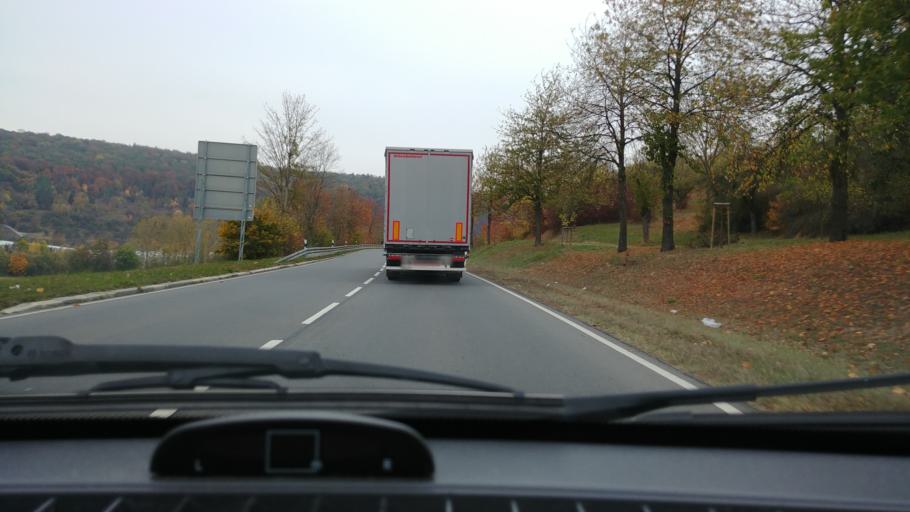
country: DE
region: Baden-Wuerttemberg
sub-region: Regierungsbezirk Stuttgart
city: Bad Mergentheim
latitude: 49.5033
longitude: 9.7561
